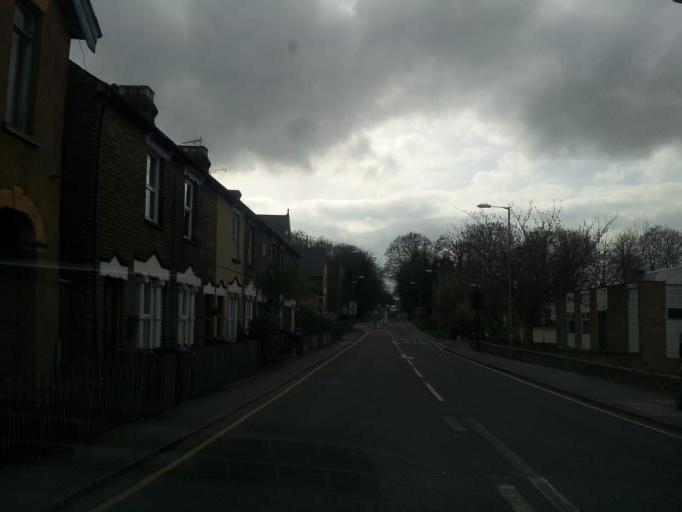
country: GB
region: England
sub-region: Hertfordshire
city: Hoddesdon
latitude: 51.7876
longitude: 0.0011
